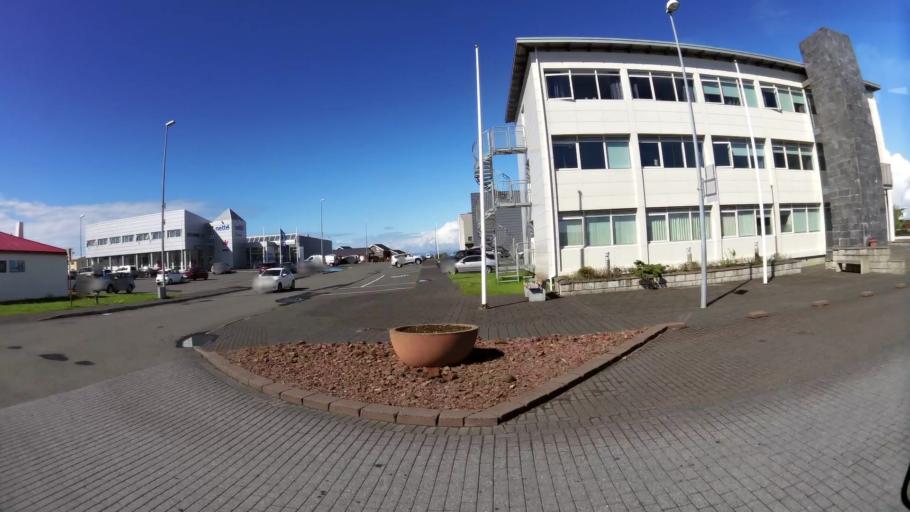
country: IS
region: East
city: Hoefn
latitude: 64.2530
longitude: -15.2110
